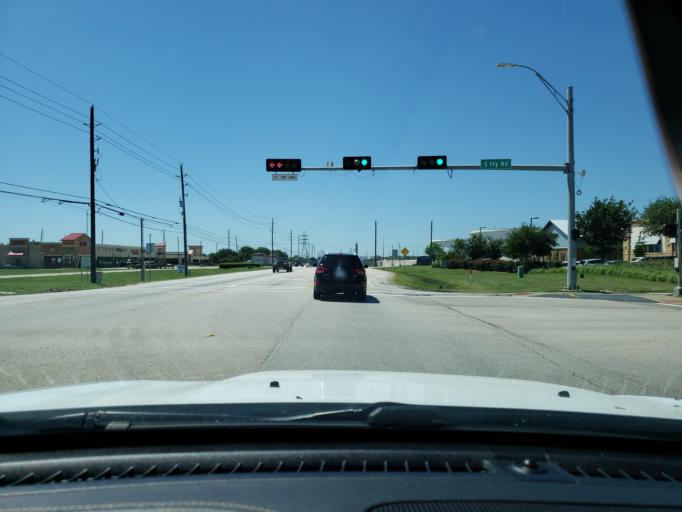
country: US
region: Texas
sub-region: Fort Bend County
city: Fulshear
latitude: 29.7065
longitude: -95.8461
